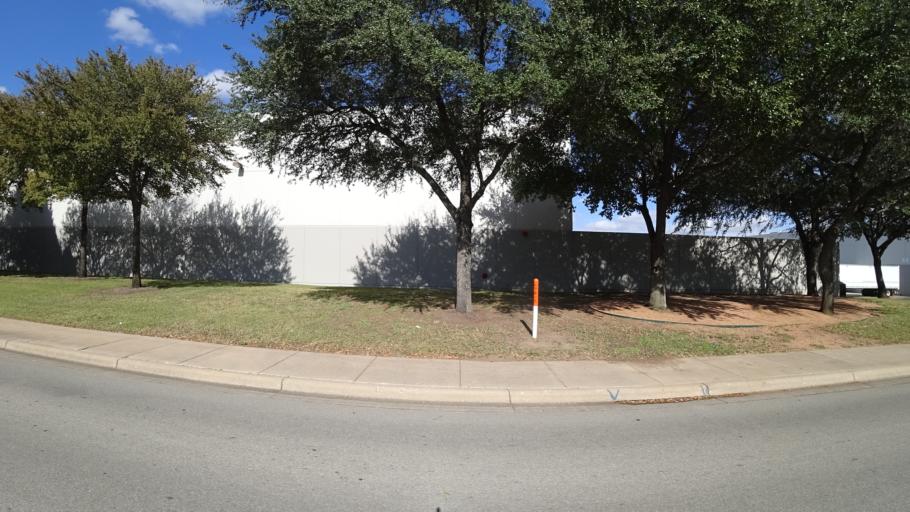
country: US
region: Texas
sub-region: Travis County
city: Wells Branch
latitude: 30.4755
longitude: -97.6765
